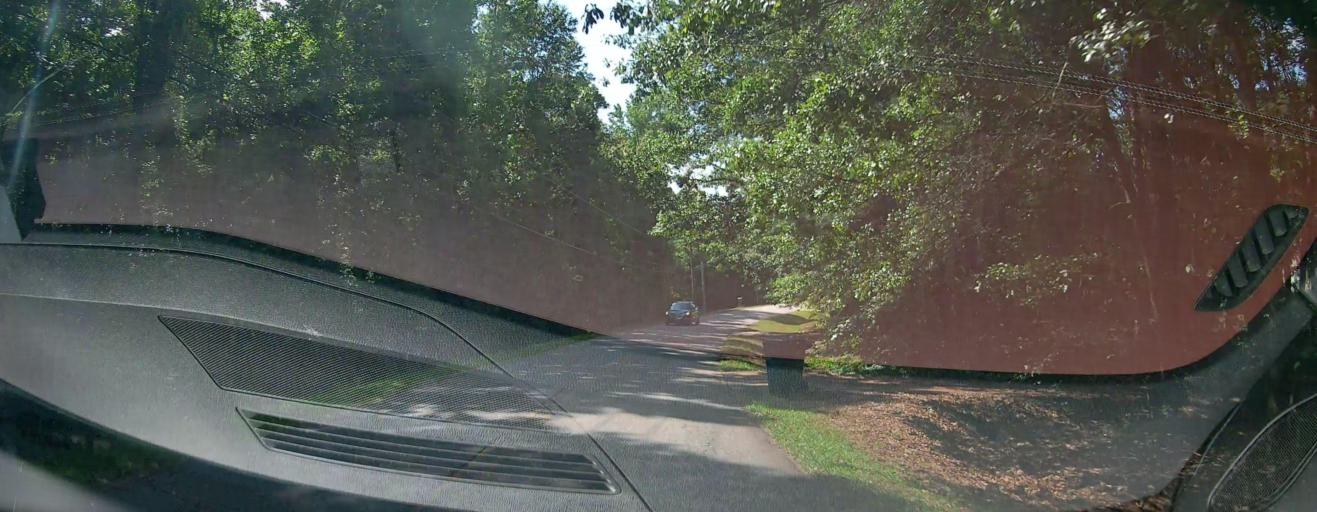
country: US
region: Georgia
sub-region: Spalding County
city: East Griffin
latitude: 33.2281
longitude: -84.1272
